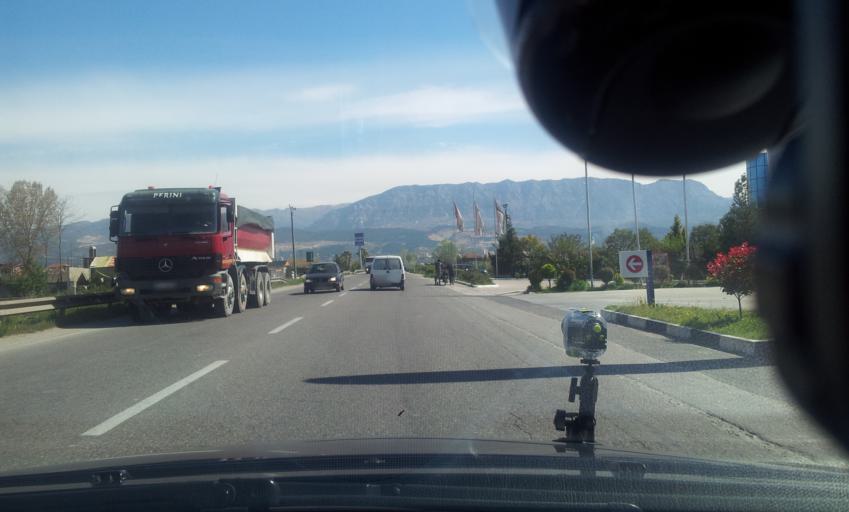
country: AL
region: Durres
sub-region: Rrethi i Krujes
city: Hasan
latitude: 41.4686
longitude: 19.6960
